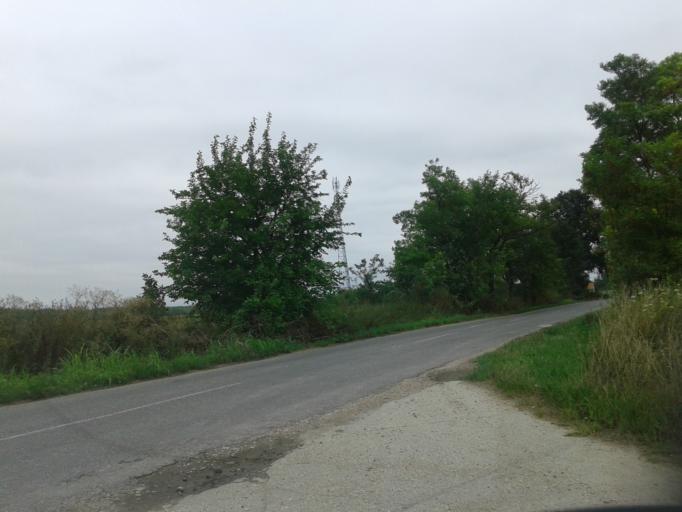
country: HU
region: Bacs-Kiskun
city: Tass
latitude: 47.0198
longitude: 19.0056
